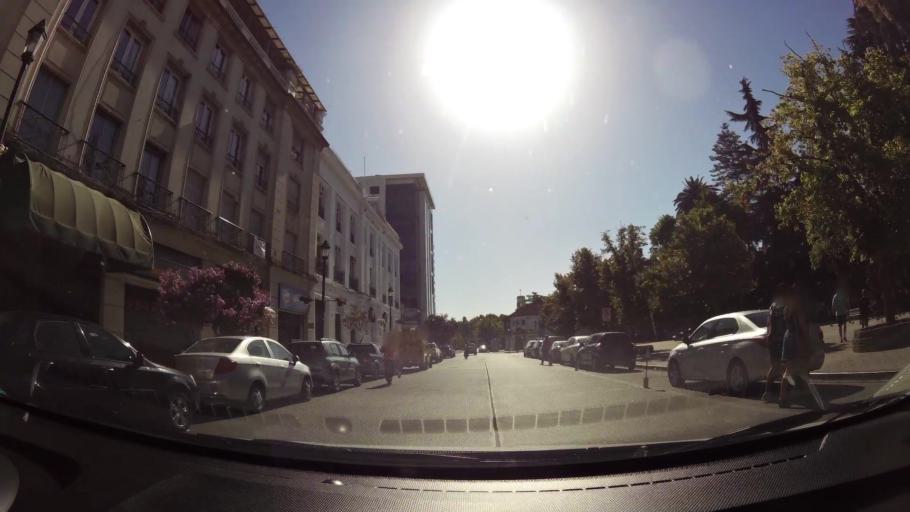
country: CL
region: Maule
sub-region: Provincia de Talca
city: Talca
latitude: -35.4271
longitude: -71.6659
